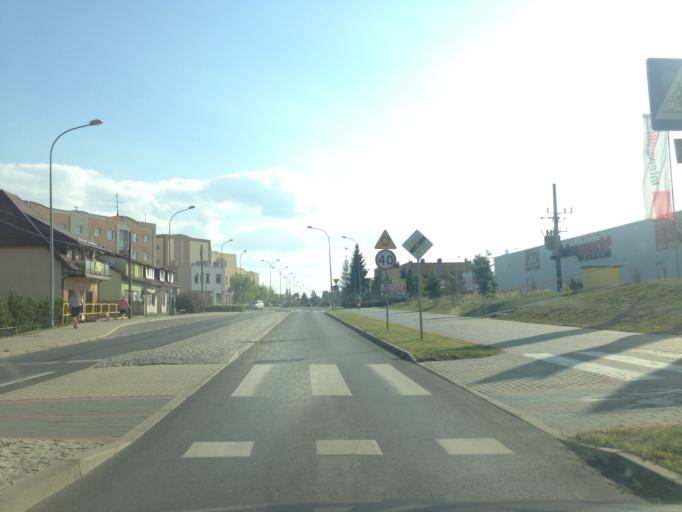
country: PL
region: Warmian-Masurian Voivodeship
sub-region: Powiat ilawski
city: Ilawa
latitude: 53.6058
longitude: 19.5679
